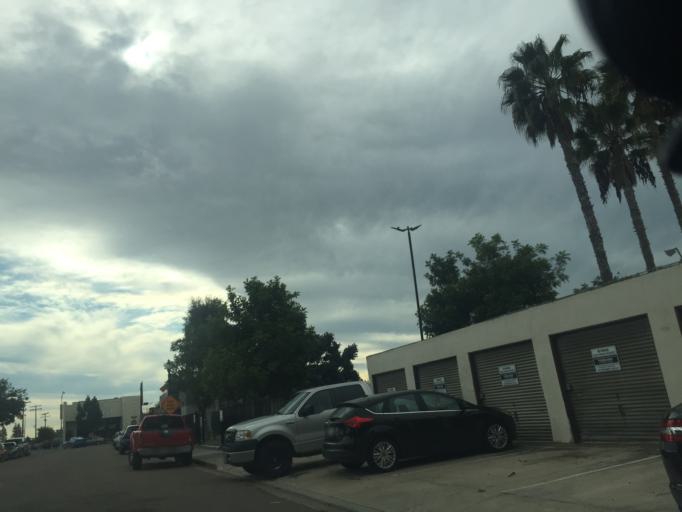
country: US
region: California
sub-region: San Diego County
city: Lemon Grove
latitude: 32.7586
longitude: -117.0809
